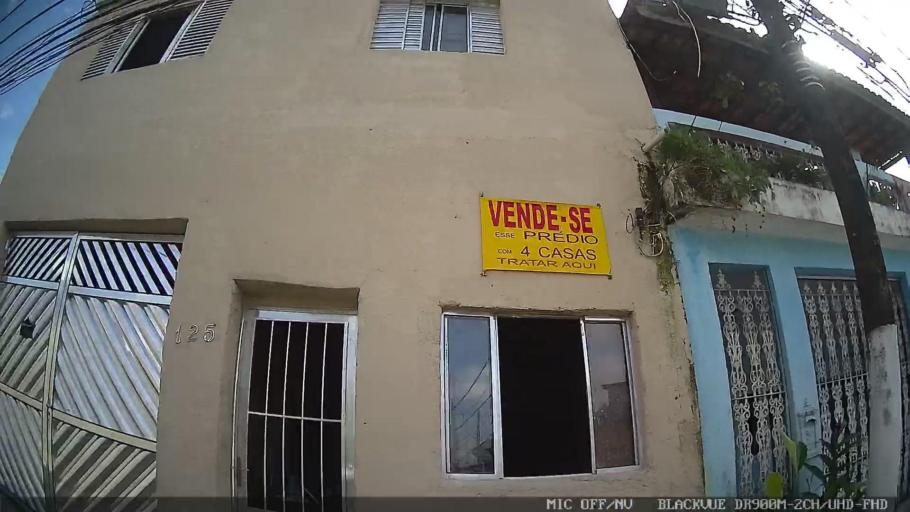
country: BR
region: Sao Paulo
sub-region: Santos
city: Santos
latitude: -23.9521
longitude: -46.2886
